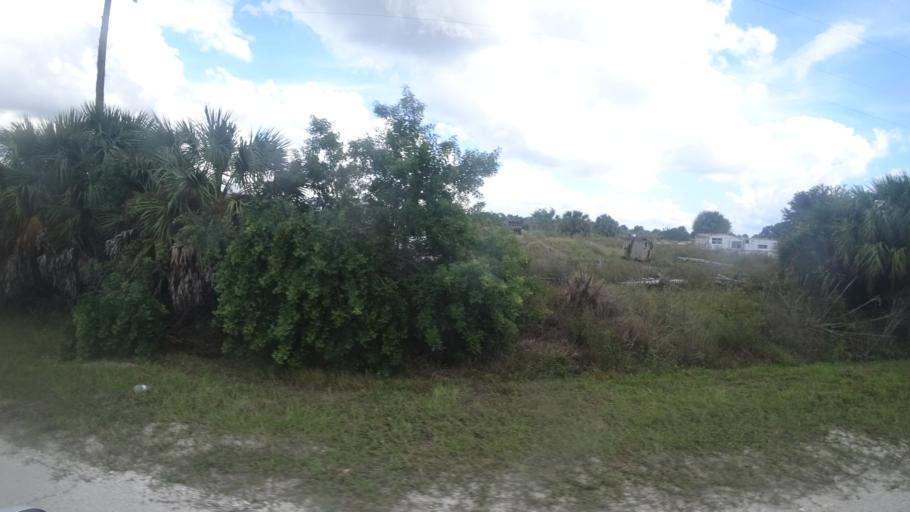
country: US
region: Florida
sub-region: Manatee County
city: Memphis
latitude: 27.6213
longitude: -82.5151
